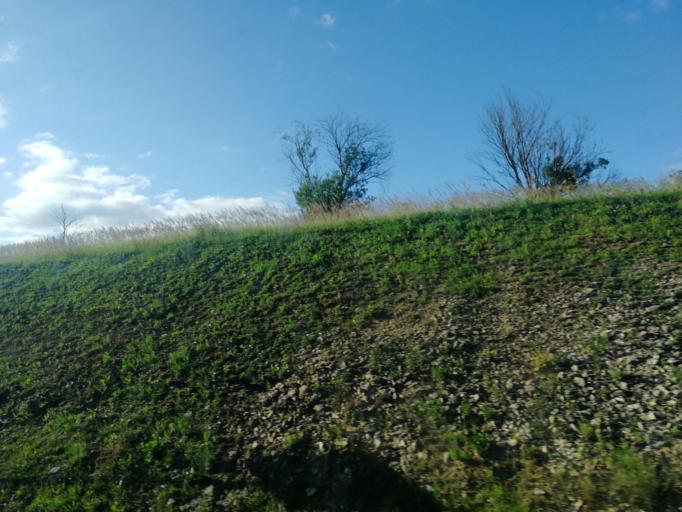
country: RU
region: Tula
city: Dubna
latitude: 54.2817
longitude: 37.1670
